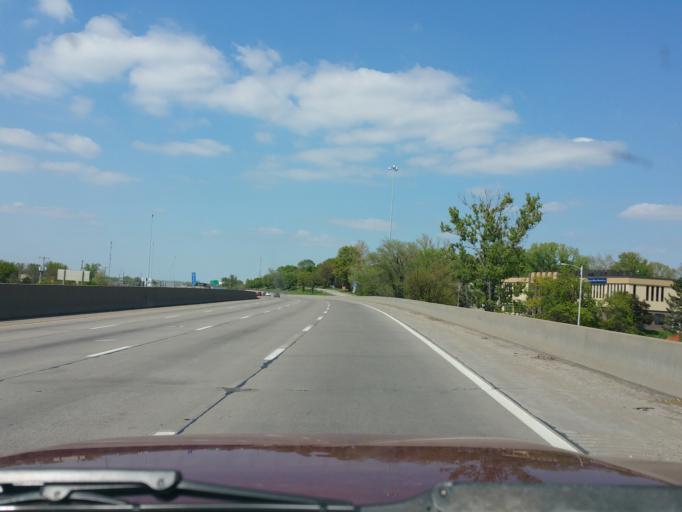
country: US
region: Kansas
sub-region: Johnson County
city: Merriam
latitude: 38.9957
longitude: -94.6957
